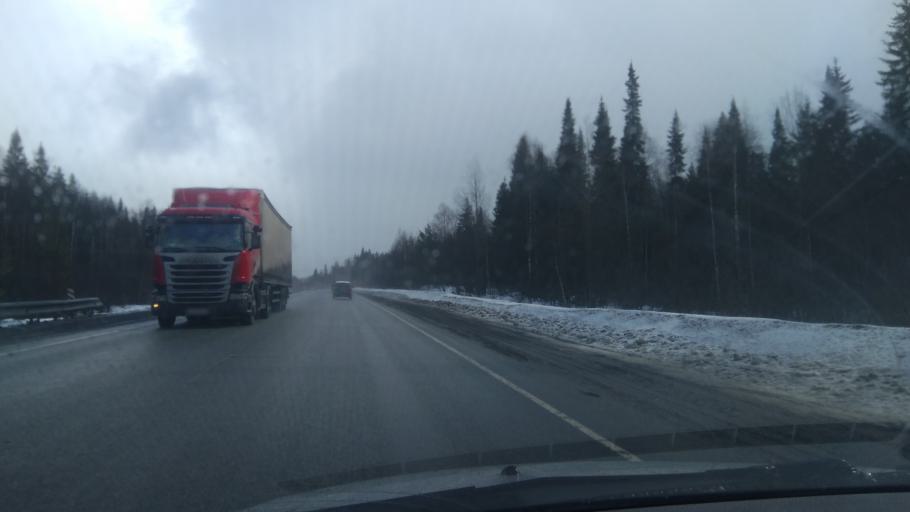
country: RU
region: Sverdlovsk
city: Arti
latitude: 56.7874
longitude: 58.5120
